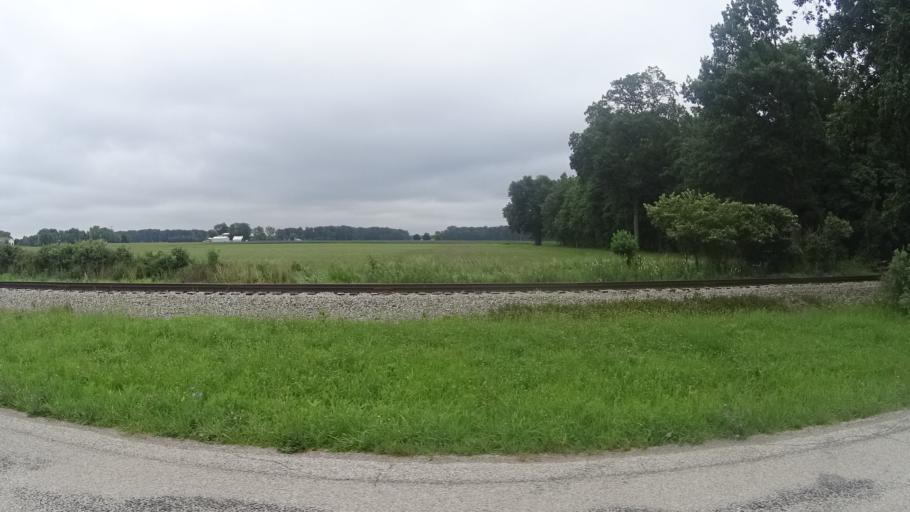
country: US
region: Ohio
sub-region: Erie County
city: Huron
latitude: 41.3544
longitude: -82.5443
